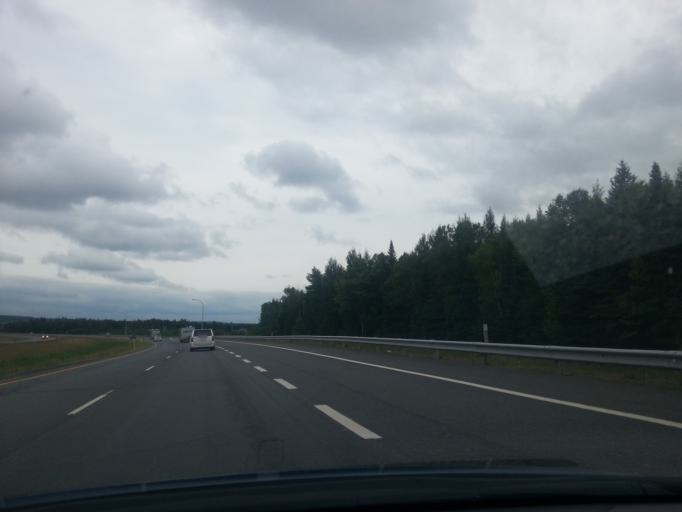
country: US
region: Maine
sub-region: Aroostook County
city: Madawaska
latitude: 47.3333
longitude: -68.1475
